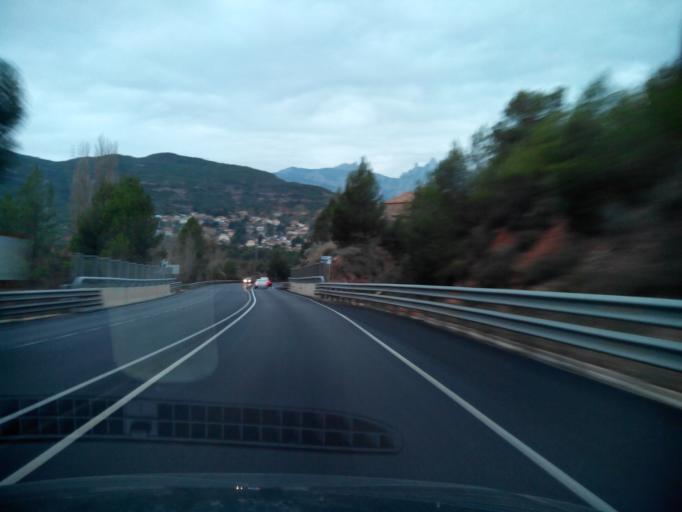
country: ES
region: Catalonia
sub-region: Provincia de Barcelona
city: Olesa de Montserrat
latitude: 41.5911
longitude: 1.9036
